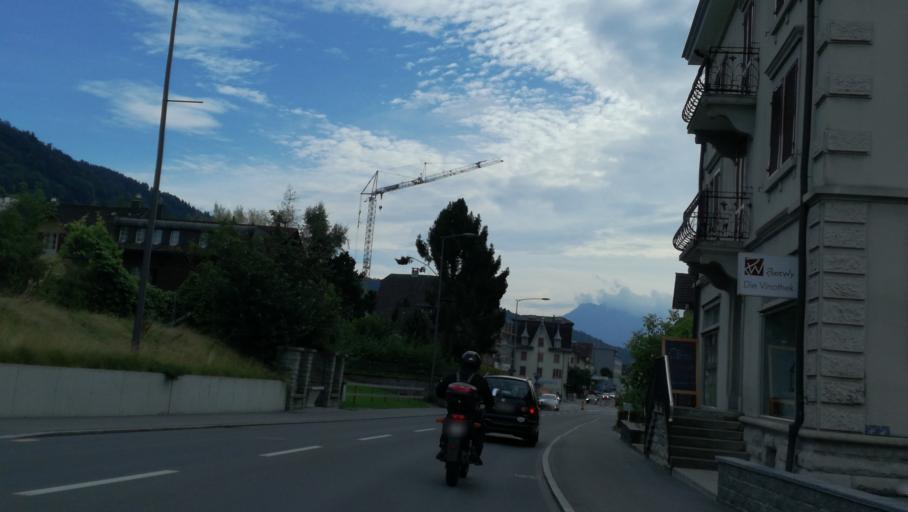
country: CH
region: Lucerne
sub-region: Lucerne-Land District
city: Root
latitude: 47.1141
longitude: 8.3893
